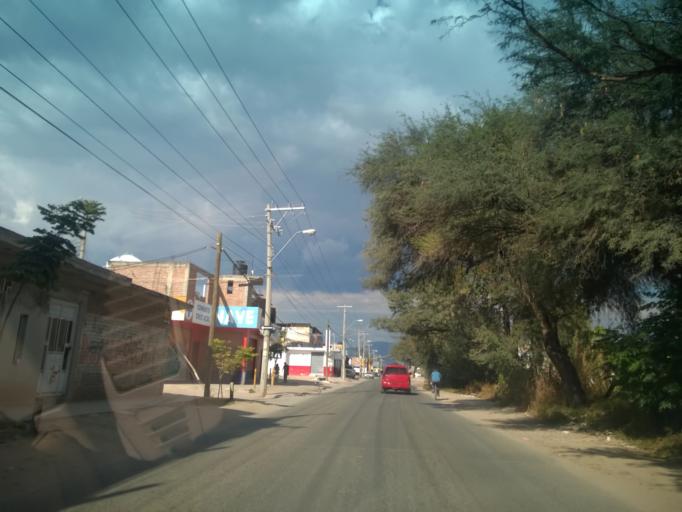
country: MX
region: Guanajuato
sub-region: Leon
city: San Jose de Duran (Los Troncoso)
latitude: 21.0661
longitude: -101.6248
